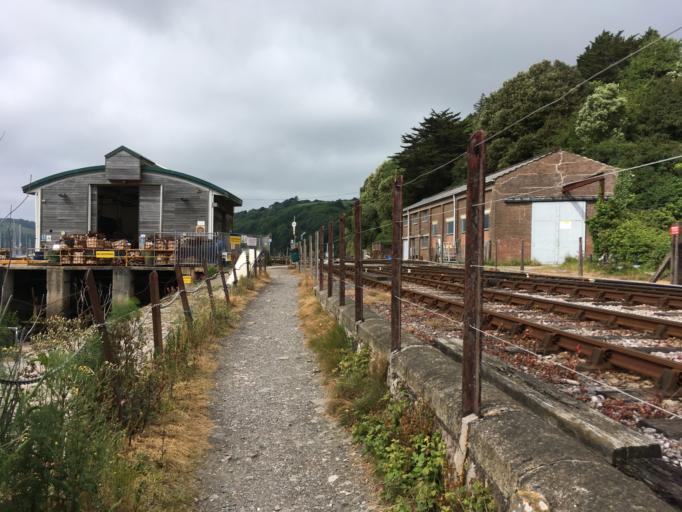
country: GB
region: England
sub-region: Devon
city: Dartmouth
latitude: 50.3514
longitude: -3.5702
